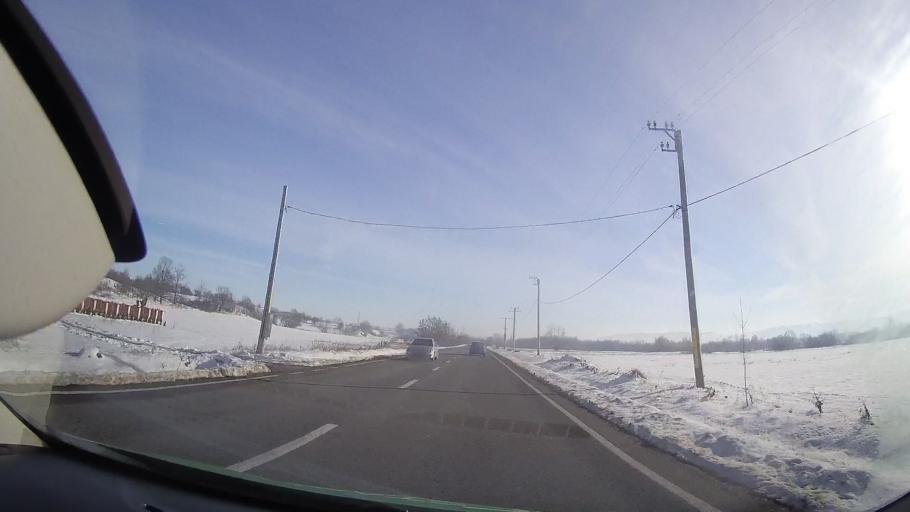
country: RO
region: Neamt
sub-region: Comuna Ghindaoani
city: Ghindaoani
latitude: 47.0779
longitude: 26.3499
